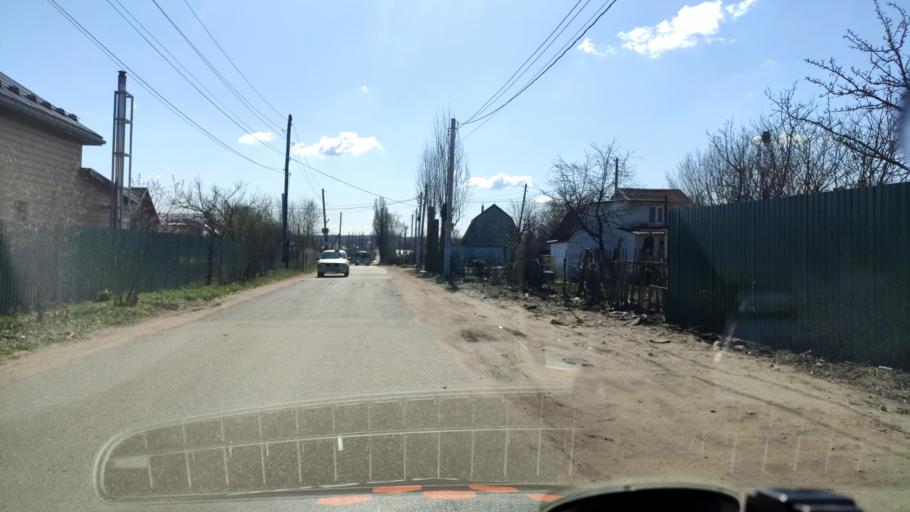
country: RU
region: Voronezj
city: Shilovo
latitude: 51.5988
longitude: 39.1461
